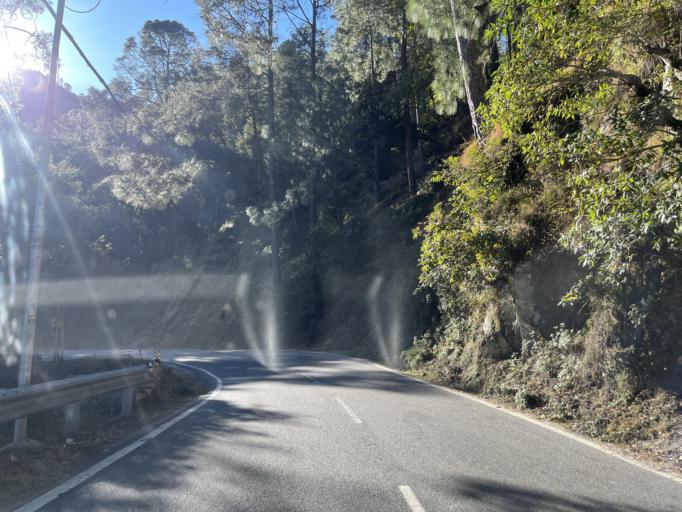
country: IN
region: Uttarakhand
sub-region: Naini Tal
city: Bhowali
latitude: 29.4049
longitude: 79.5121
